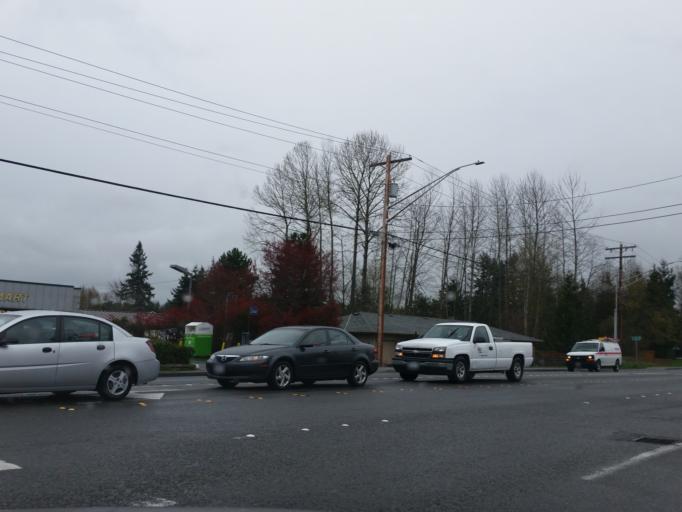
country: US
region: Washington
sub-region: Snohomish County
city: Martha Lake
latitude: 47.8964
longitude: -122.2387
